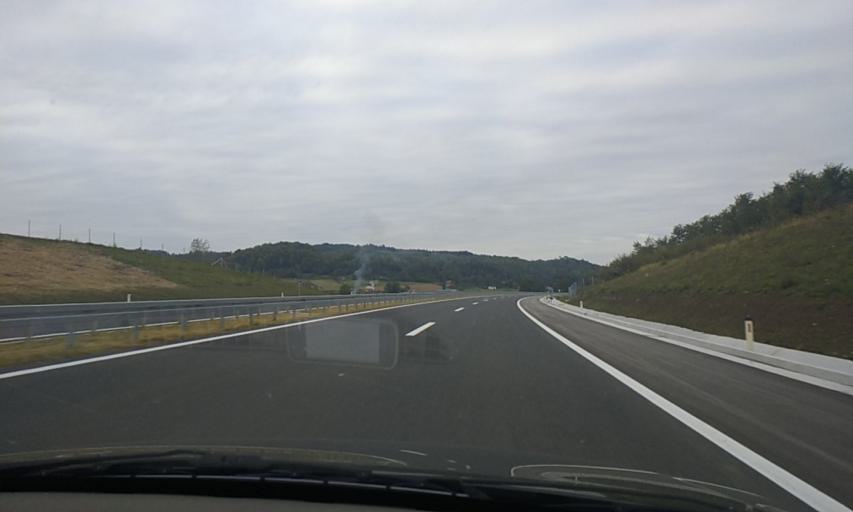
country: BA
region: Republika Srpska
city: Maglajani
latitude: 44.8550
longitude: 17.4479
